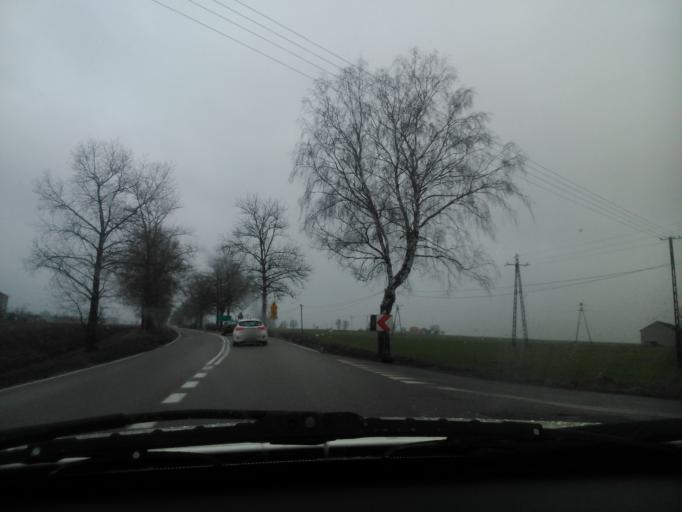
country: PL
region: Kujawsko-Pomorskie
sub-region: Powiat brodnicki
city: Bobrowo
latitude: 53.2259
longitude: 19.2047
